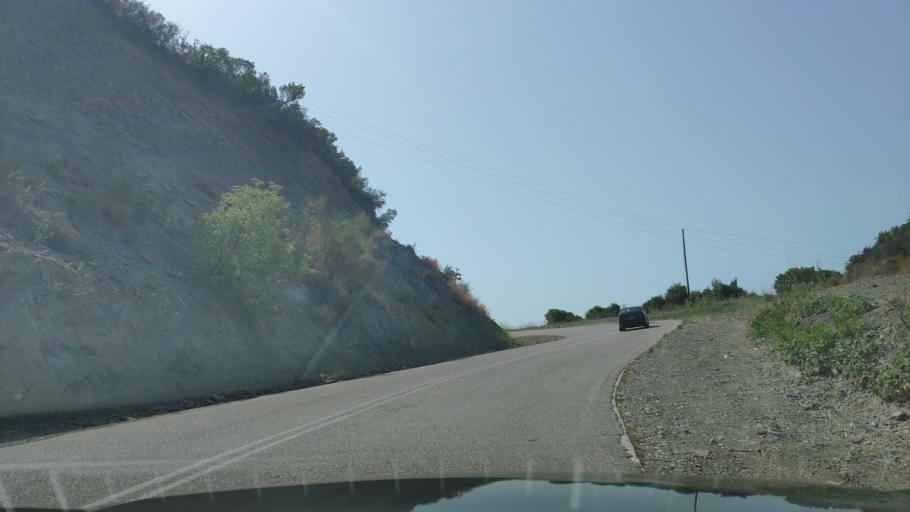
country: GR
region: Epirus
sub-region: Nomos Artas
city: Peta
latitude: 39.1690
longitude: 21.0640
